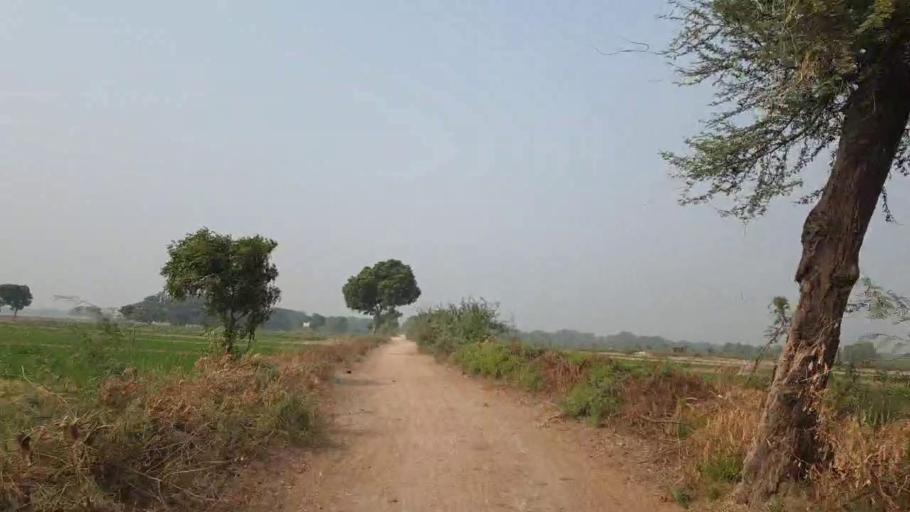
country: PK
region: Sindh
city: Tando Muhammad Khan
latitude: 25.2019
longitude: 68.5637
